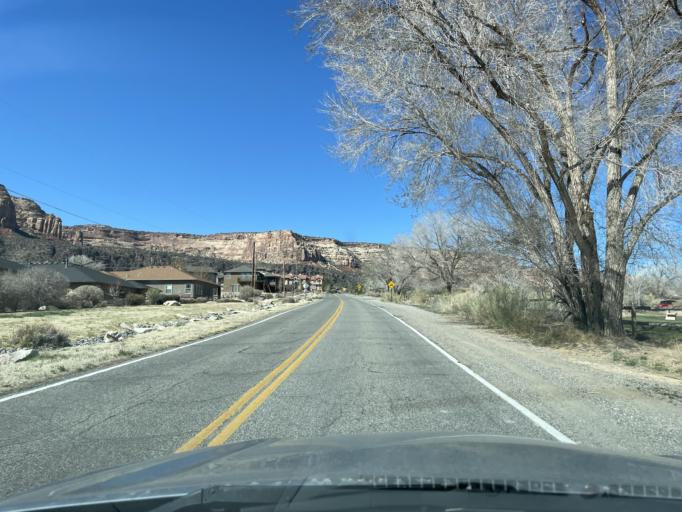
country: US
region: Colorado
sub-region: Mesa County
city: Redlands
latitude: 39.0779
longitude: -108.6651
